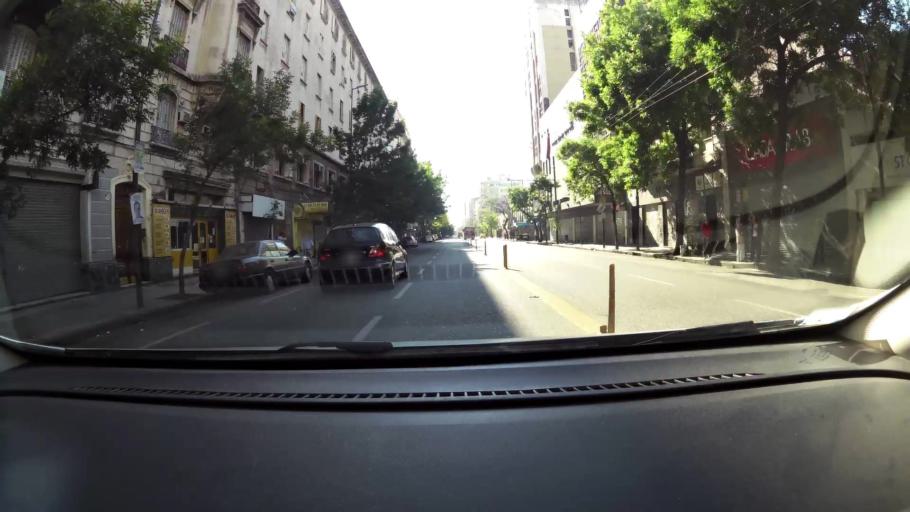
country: AR
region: Cordoba
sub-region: Departamento de Capital
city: Cordoba
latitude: -31.4135
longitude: -64.1837
